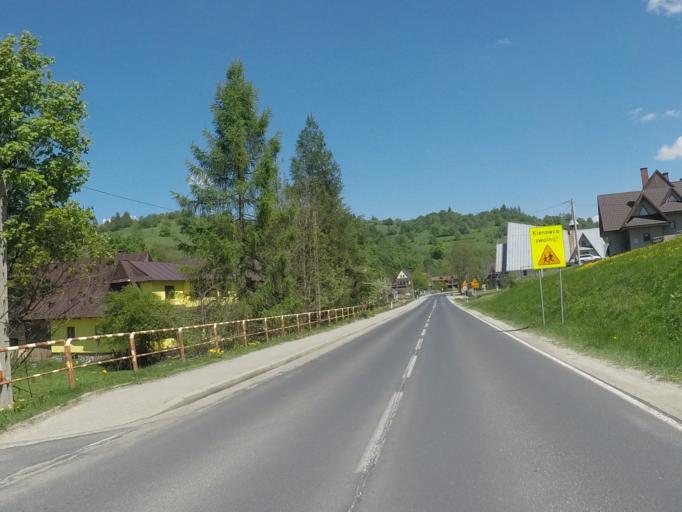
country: PL
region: Lesser Poland Voivodeship
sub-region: Powiat tatrzanski
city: Bukowina Tatrzanska
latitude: 49.3363
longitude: 20.0568
